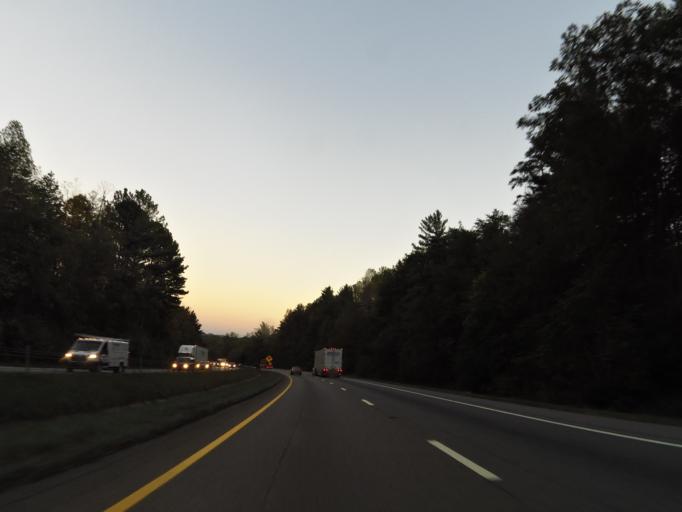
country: US
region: Tennessee
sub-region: Campbell County
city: Caryville
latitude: 36.2659
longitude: -84.1939
